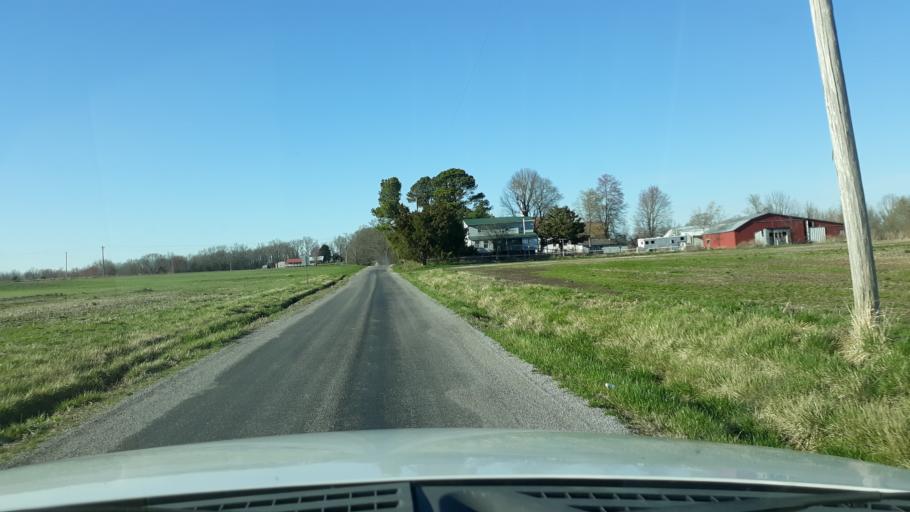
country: US
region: Illinois
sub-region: Saline County
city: Harrisburg
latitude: 37.8029
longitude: -88.6055
